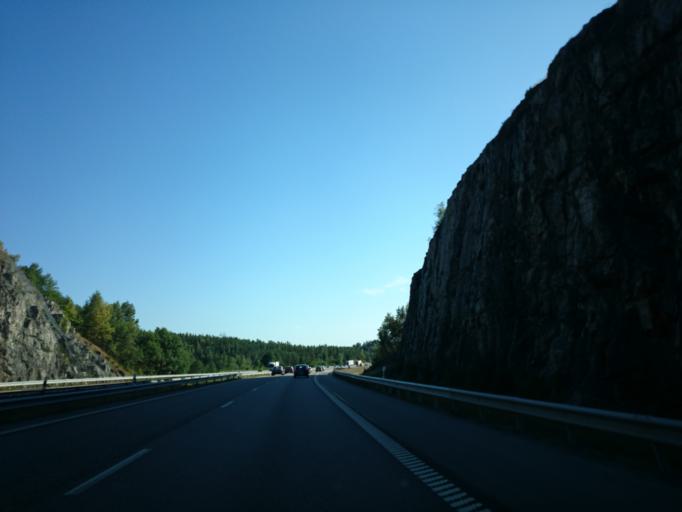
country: SE
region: Stockholm
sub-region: Sodertalje Kommun
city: Pershagen
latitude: 59.1329
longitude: 17.6443
